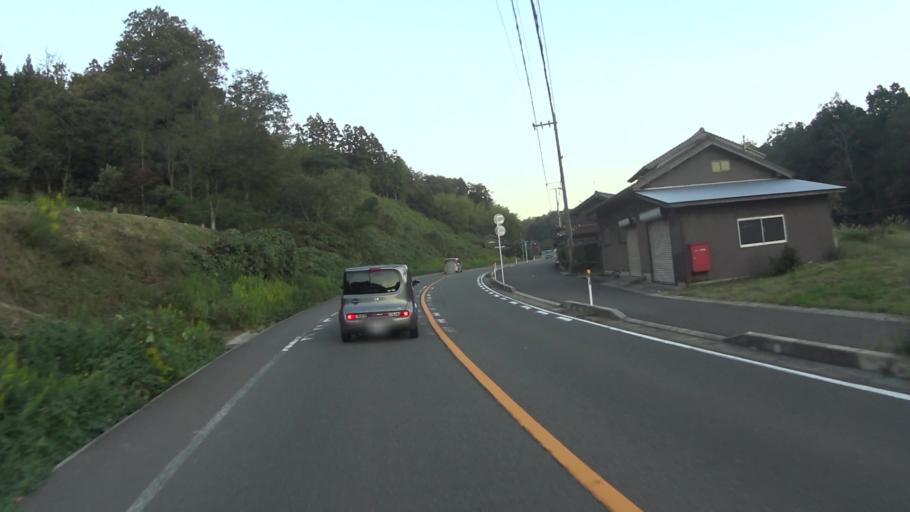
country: JP
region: Kyoto
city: Miyazu
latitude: 35.6485
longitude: 135.0424
